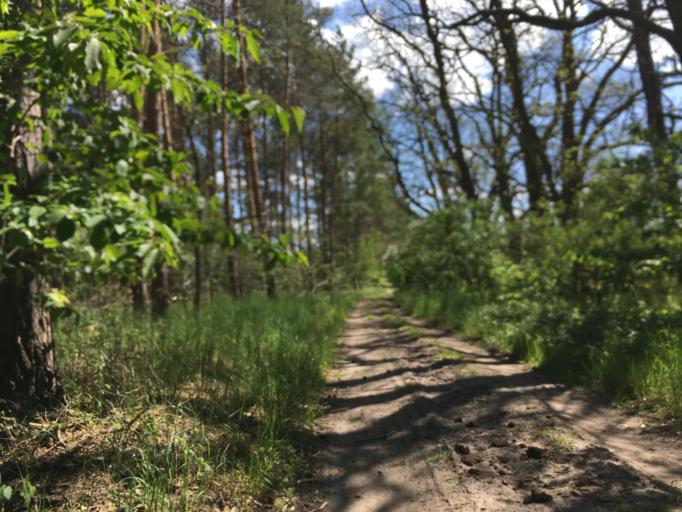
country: DE
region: Brandenburg
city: Rudnitz
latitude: 52.7149
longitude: 13.6578
